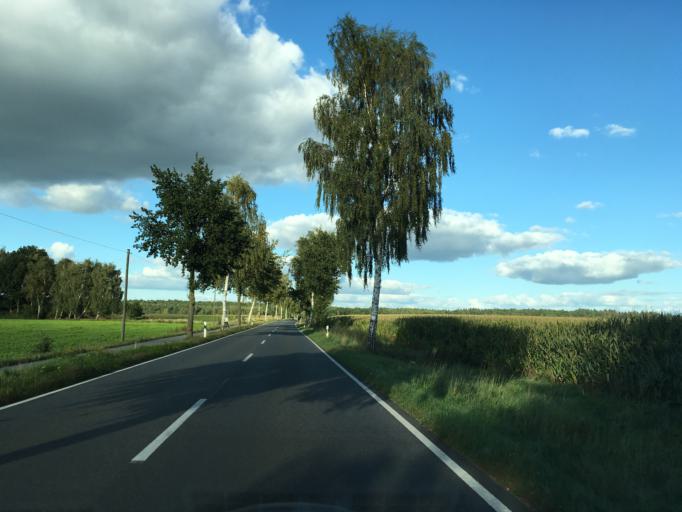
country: DE
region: Lower Saxony
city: Kirchgellersen
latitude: 53.2331
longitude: 10.3056
